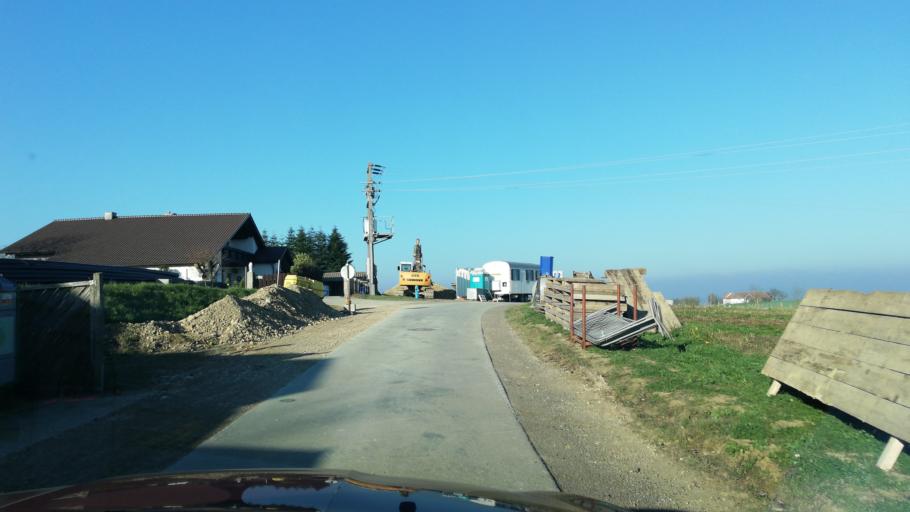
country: AT
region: Upper Austria
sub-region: Wels-Land
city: Buchkirchen
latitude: 48.2508
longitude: 14.0196
